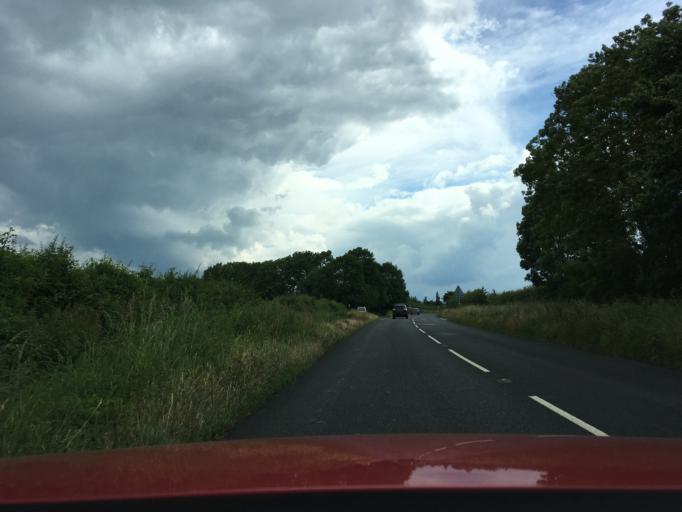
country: GB
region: England
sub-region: Gloucestershire
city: Stonehouse
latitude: 51.7866
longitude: -2.2895
